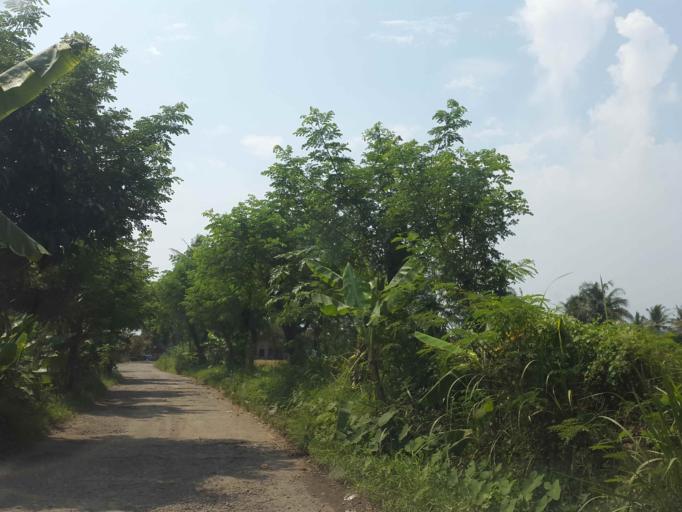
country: ID
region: West Java
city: Ciranjang-hilir
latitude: -6.7996
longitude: 107.2836
